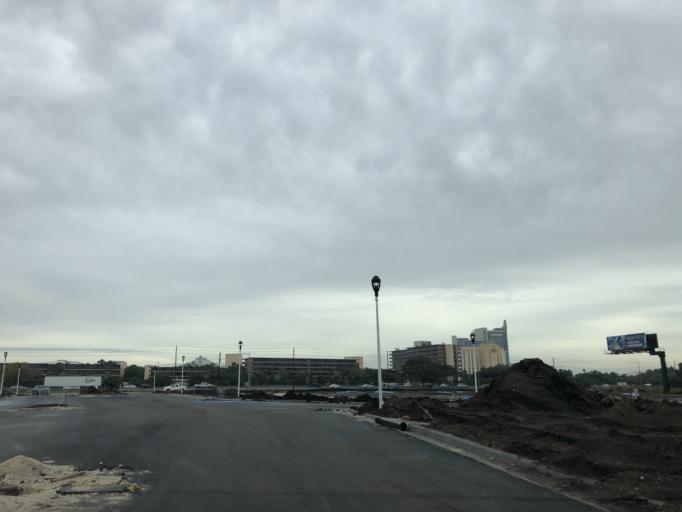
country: US
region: Florida
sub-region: Orange County
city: Doctor Phillips
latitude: 28.4337
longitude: -81.4765
